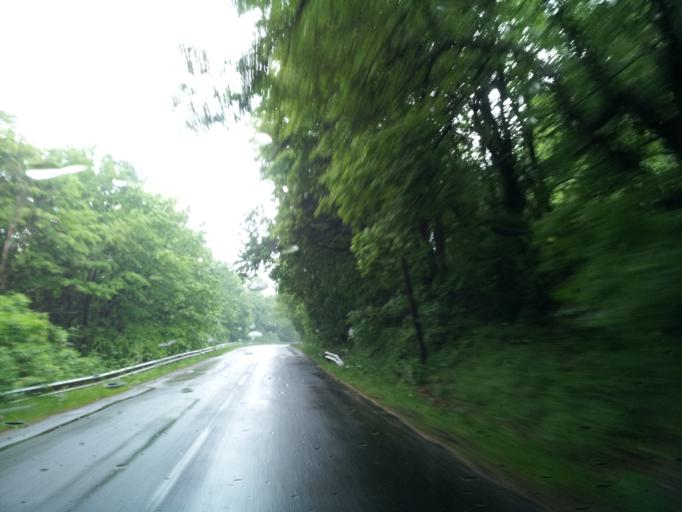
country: HU
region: Baranya
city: Hosszuheteny
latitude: 46.1779
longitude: 18.3205
